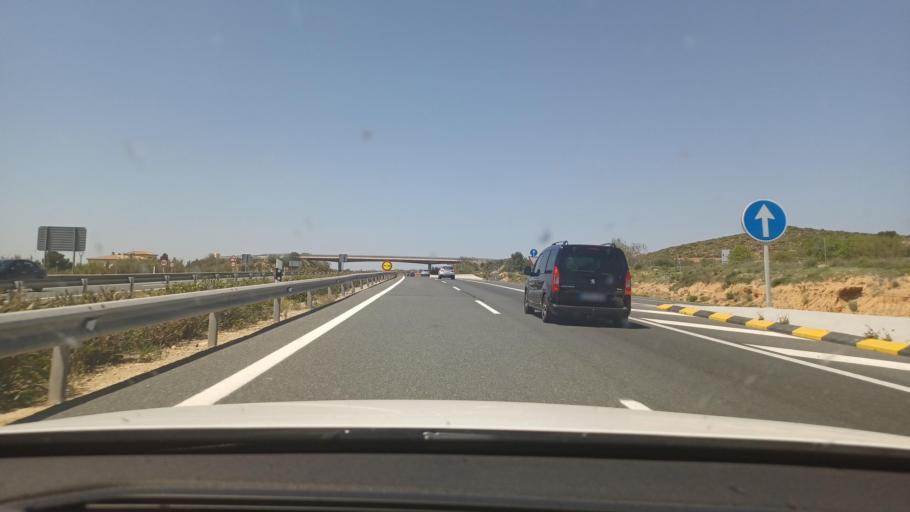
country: ES
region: Castille-La Mancha
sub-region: Provincia de Albacete
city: Almansa
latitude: 38.8780
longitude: -1.1705
